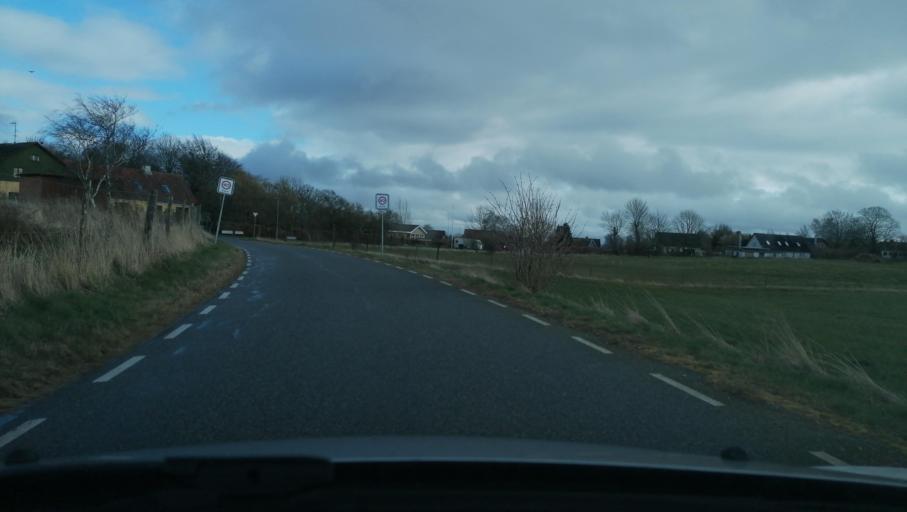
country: DK
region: Zealand
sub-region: Odsherred Kommune
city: Horve
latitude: 55.7424
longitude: 11.4013
